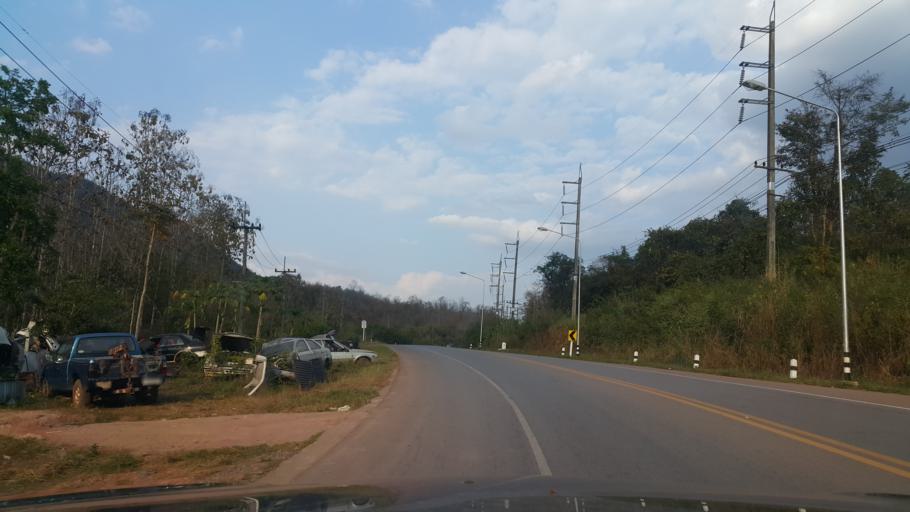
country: TH
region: Loei
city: Dan Sai
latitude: 17.2992
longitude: 101.1956
